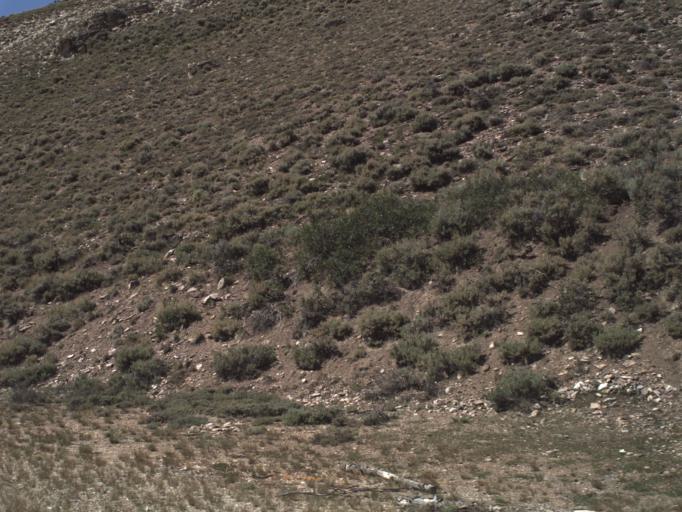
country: US
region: Utah
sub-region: Rich County
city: Randolph
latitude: 41.4835
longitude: -111.3914
